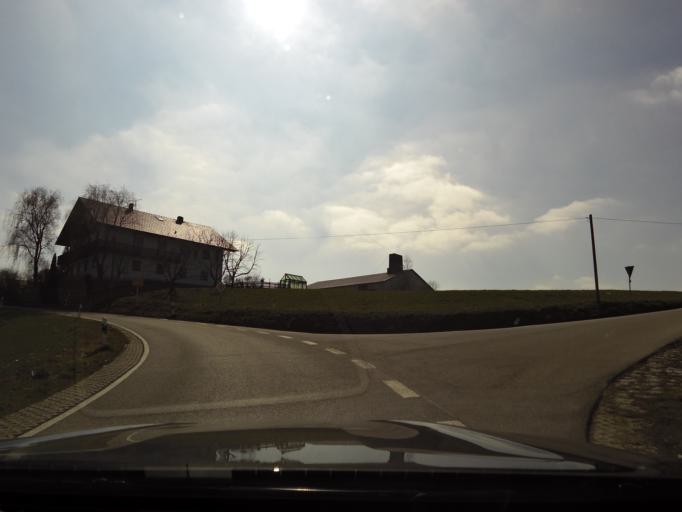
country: DE
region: Bavaria
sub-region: Lower Bavaria
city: Tiefenbach
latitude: 48.5075
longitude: 12.1094
